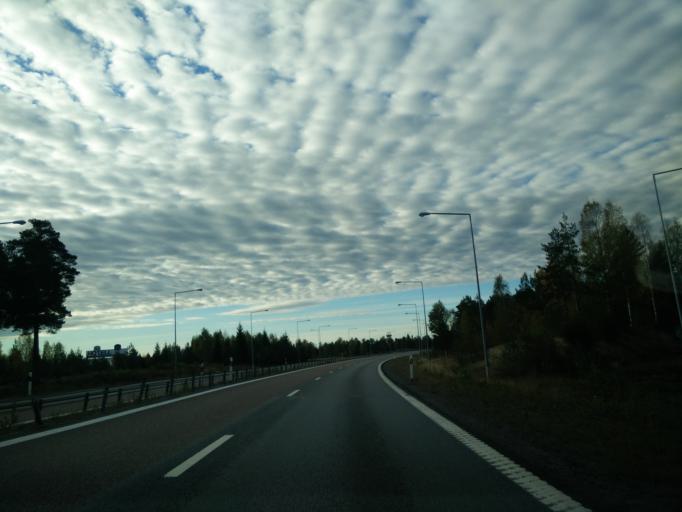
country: SE
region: Gaevleborg
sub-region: Soderhamns Kommun
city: Soderhamn
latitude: 61.3043
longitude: 17.0318
